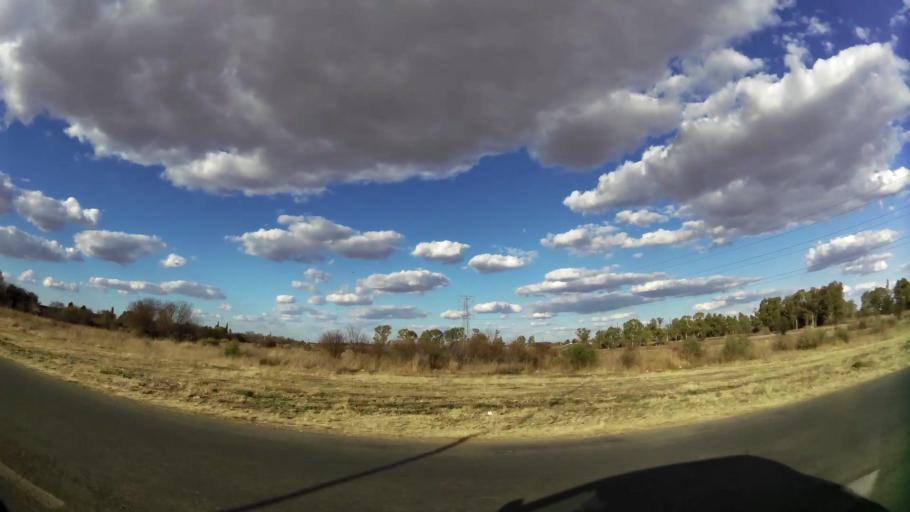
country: ZA
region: North-West
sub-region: Dr Kenneth Kaunda District Municipality
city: Potchefstroom
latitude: -26.7052
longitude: 27.0781
